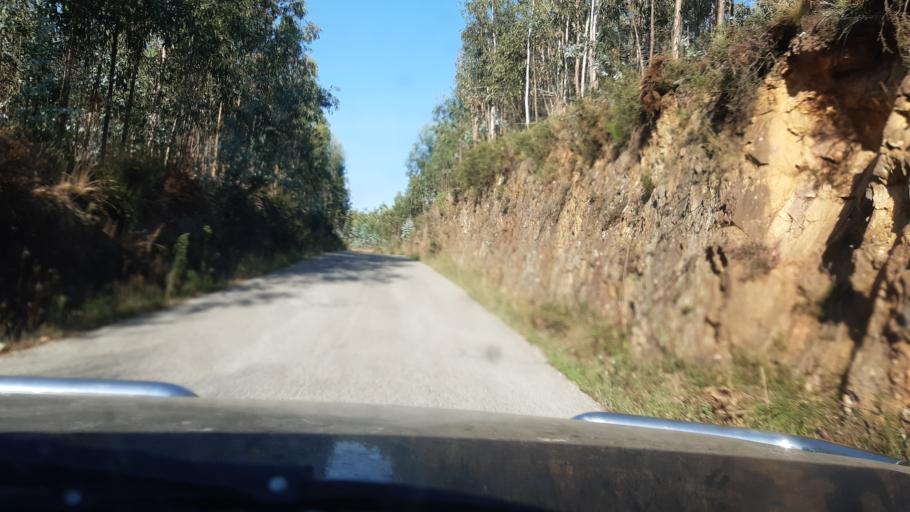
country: PT
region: Aveiro
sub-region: Agueda
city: Aguada de Cima
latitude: 40.5673
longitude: -8.3281
